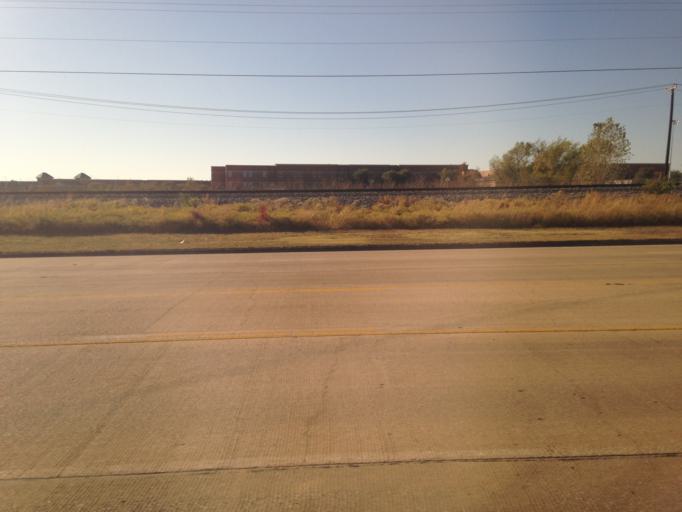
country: US
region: Texas
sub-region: Tarrant County
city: Watauga
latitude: 32.8885
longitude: -97.2596
